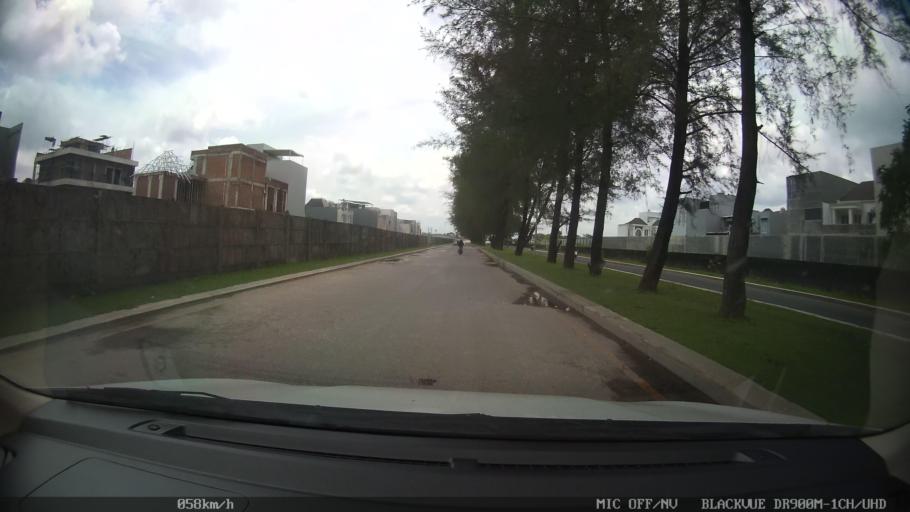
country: ID
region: North Sumatra
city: Medan
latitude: 3.6122
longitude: 98.7292
